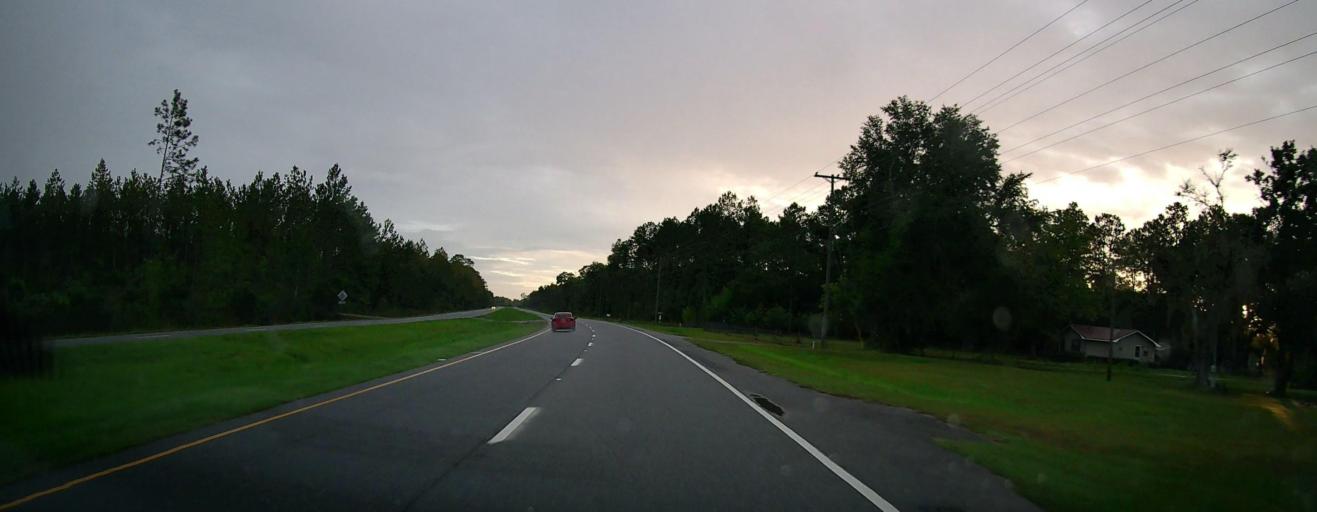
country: US
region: Georgia
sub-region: Clinch County
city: Homerville
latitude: 31.0088
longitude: -82.8510
